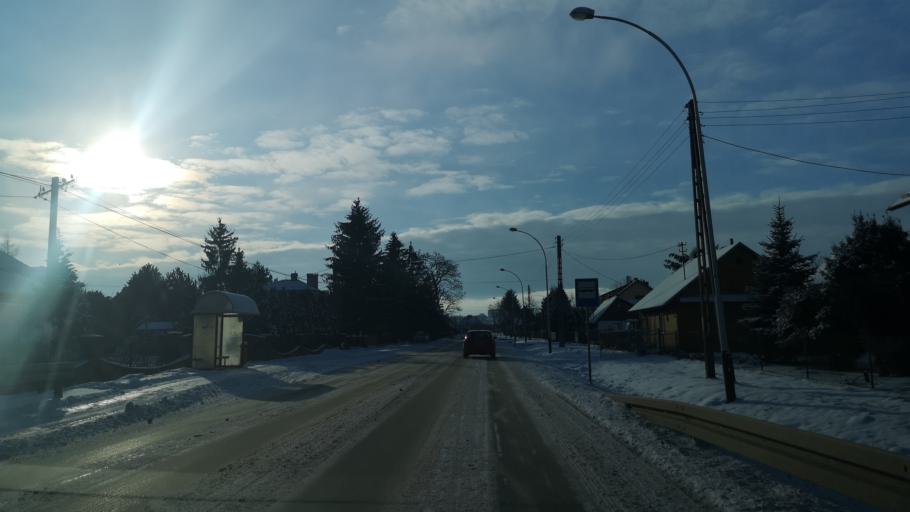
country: PL
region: Subcarpathian Voivodeship
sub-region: Powiat przeworski
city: Gorliczyna
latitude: 50.0771
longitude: 22.4935
